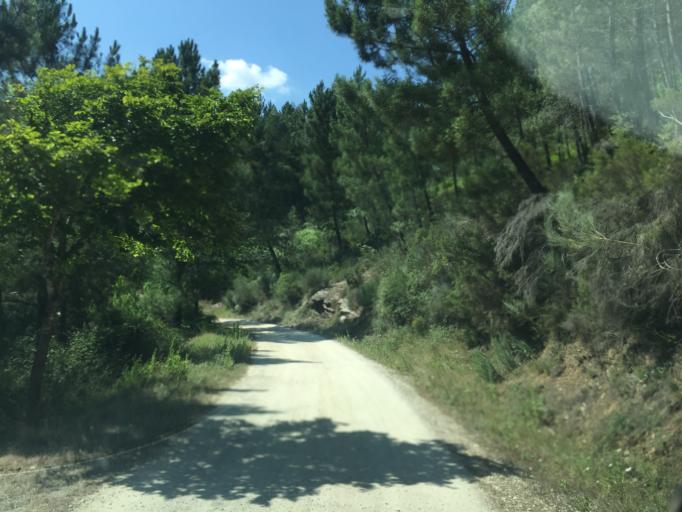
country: PT
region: Leiria
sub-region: Pedrogao Grande
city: Pedrogao Grande
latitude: 39.9289
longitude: -8.1273
